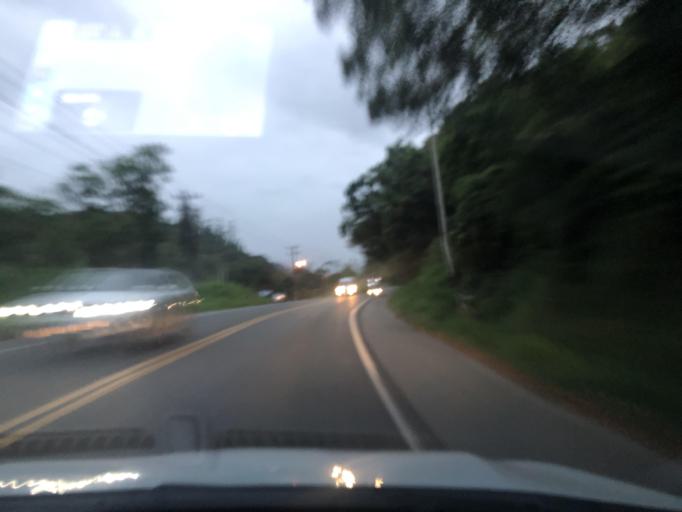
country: BR
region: Santa Catarina
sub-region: Pomerode
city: Pomerode
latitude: -26.6793
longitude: -49.0410
